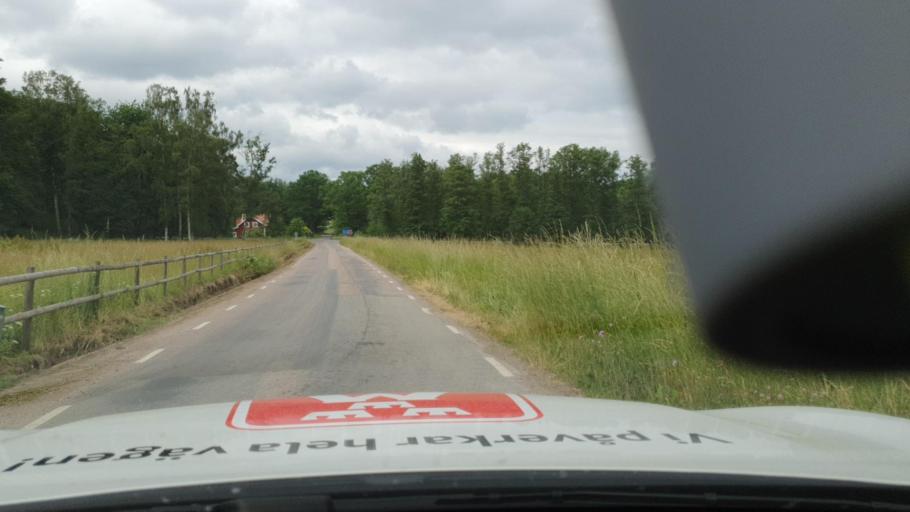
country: SE
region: Vaestra Goetaland
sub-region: Hjo Kommun
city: Hjo
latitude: 58.2244
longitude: 14.2061
